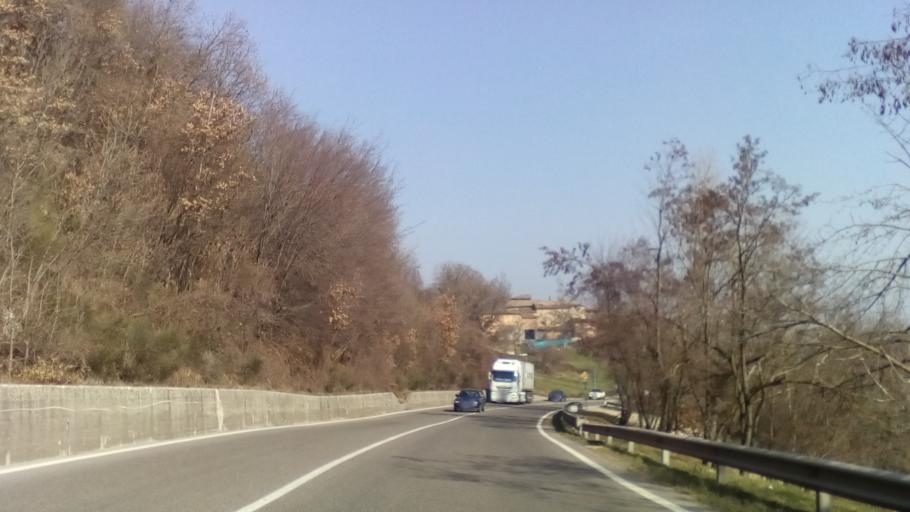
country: IT
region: Emilia-Romagna
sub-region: Provincia di Modena
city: Sant'Antonio
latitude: 44.4076
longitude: 10.8324
